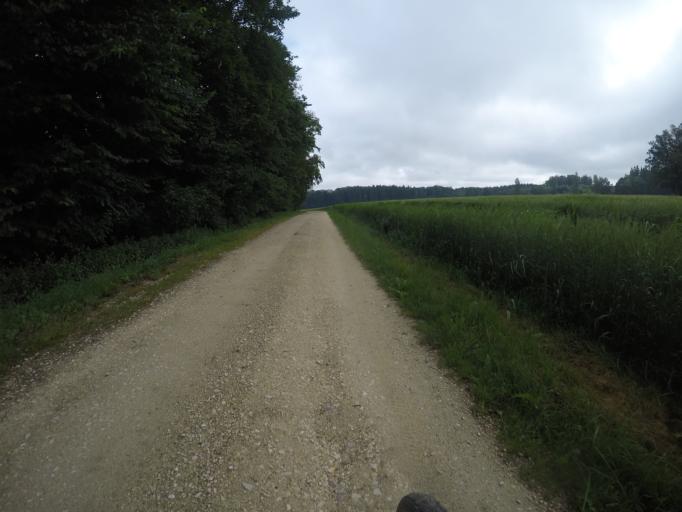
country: DE
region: Baden-Wuerttemberg
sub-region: Tuebingen Region
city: Dornstadt
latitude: 48.4784
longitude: 9.9576
